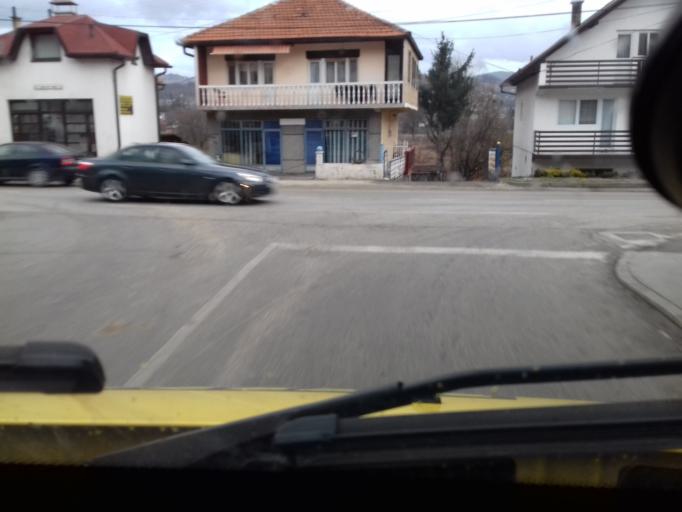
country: BA
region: Federation of Bosnia and Herzegovina
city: Vitez
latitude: 44.1465
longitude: 17.7961
